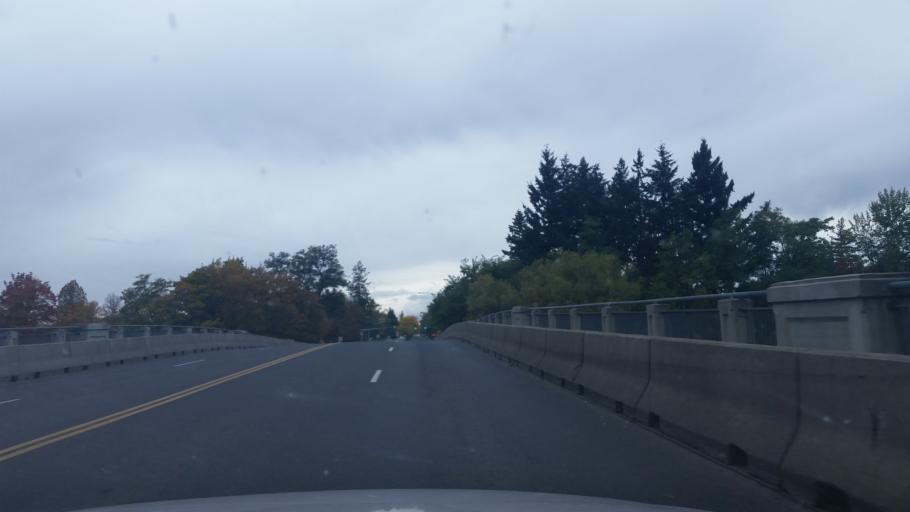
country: US
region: Washington
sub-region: Spokane County
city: Spokane
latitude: 47.6718
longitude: -117.3870
